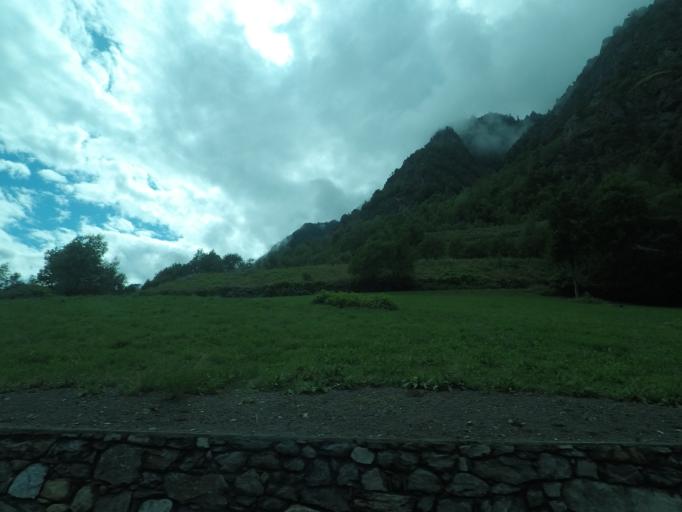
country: IT
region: Aosta Valley
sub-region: Valle d'Aosta
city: Chamois
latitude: 45.8337
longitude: 7.6009
